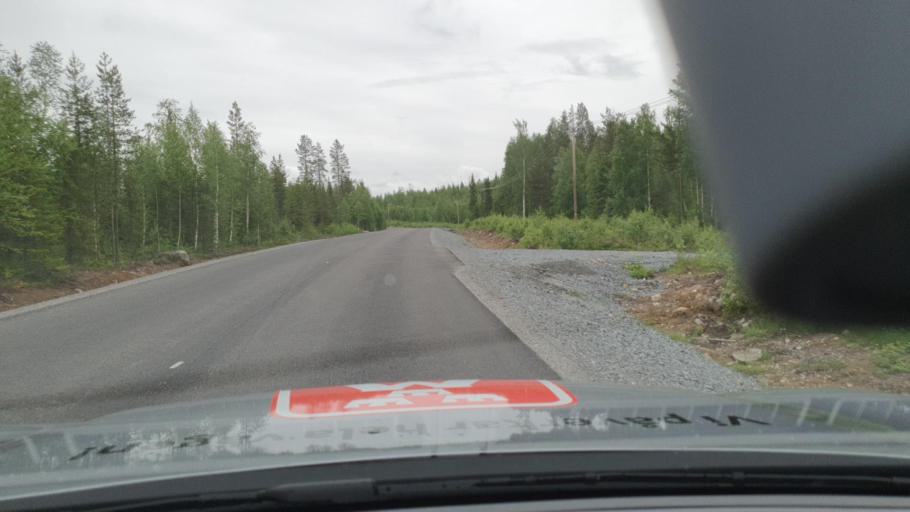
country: SE
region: Norrbotten
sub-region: Overtornea Kommun
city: OEvertornea
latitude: 66.6304
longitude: 23.2682
